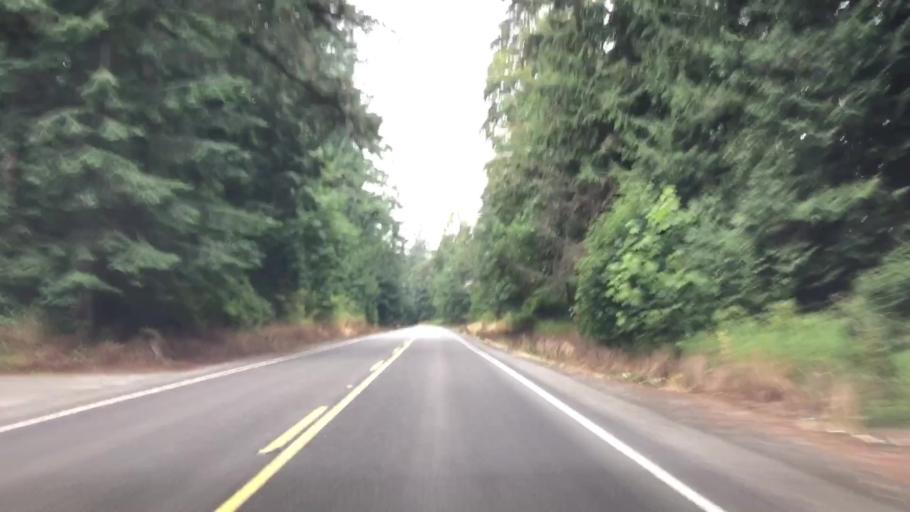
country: US
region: Washington
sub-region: Kitsap County
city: Navy Yard City
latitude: 47.5265
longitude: -122.7376
